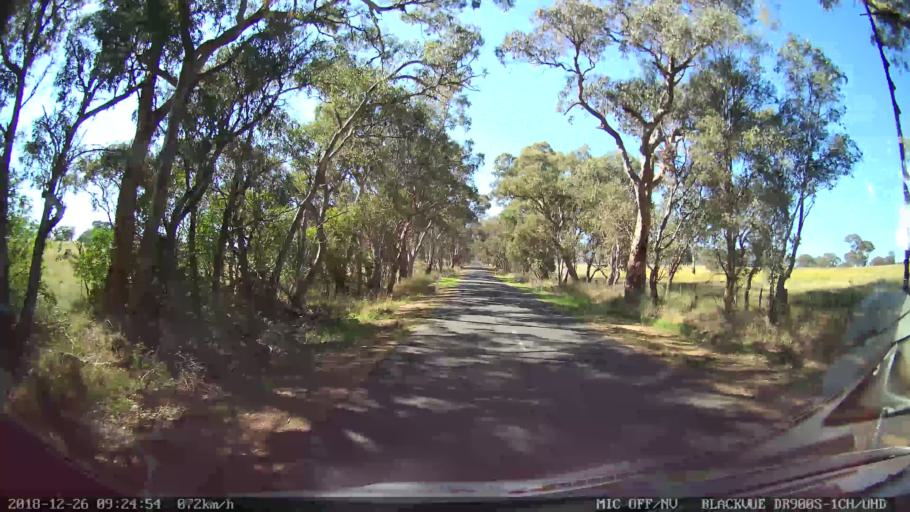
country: AU
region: New South Wales
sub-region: Mid-Western Regional
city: Kandos
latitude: -32.8147
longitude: 150.0014
